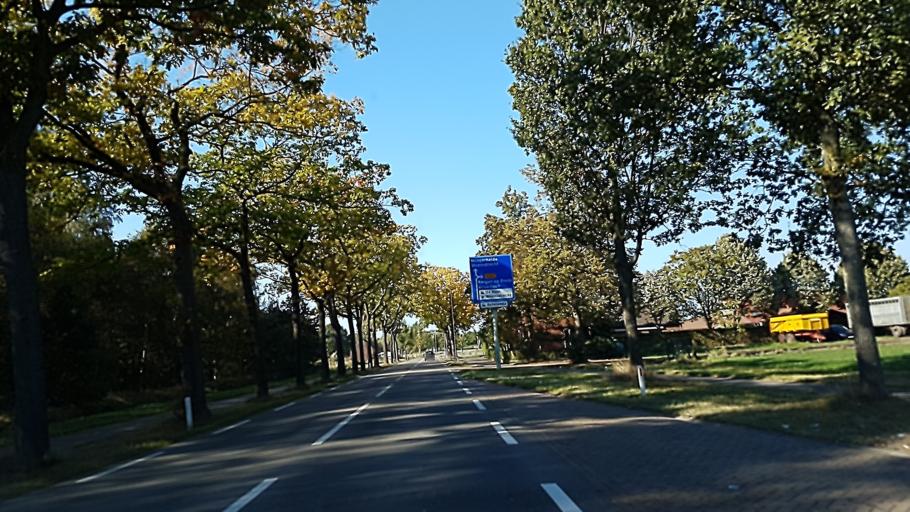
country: NL
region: North Brabant
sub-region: Gemeente Woensdrecht
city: Woensdrecht
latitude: 51.4129
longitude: 4.3426
